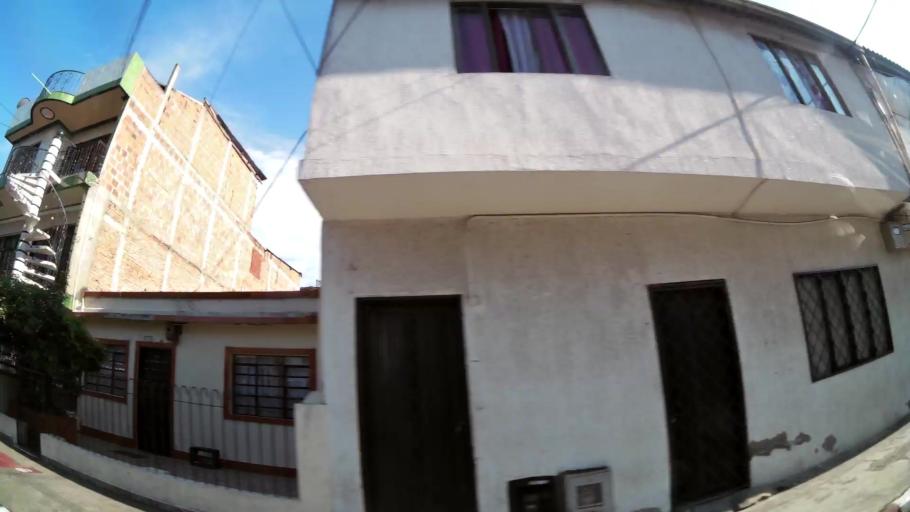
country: CO
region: Valle del Cauca
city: Cali
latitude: 3.4273
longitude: -76.5154
